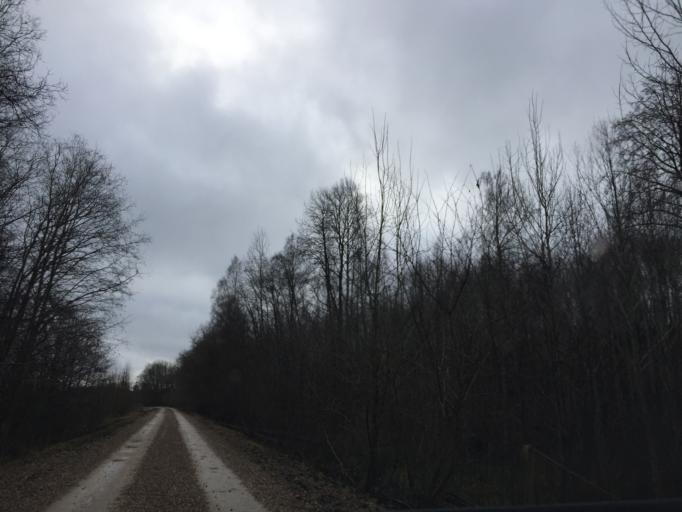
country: LV
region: Broceni
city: Broceni
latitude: 56.6789
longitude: 22.5578
